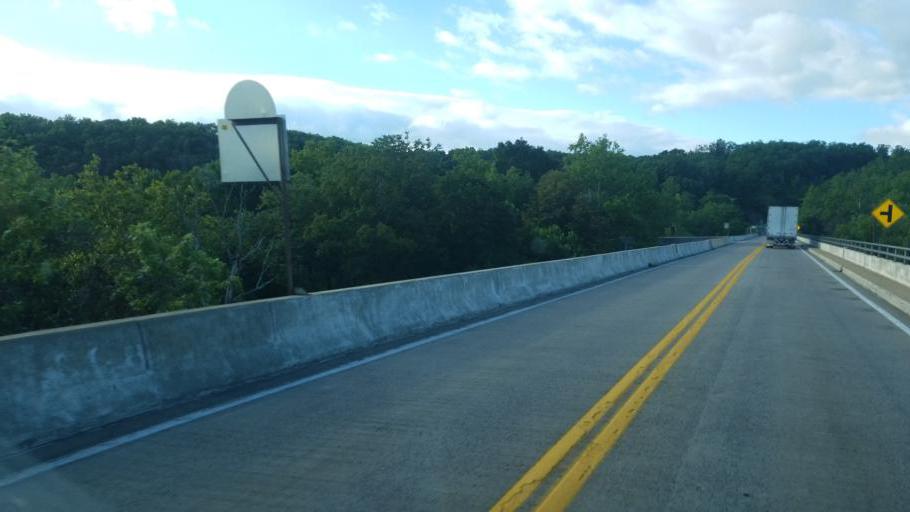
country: US
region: Maryland
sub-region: Washington County
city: Hancock
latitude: 39.6932
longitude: -78.1863
